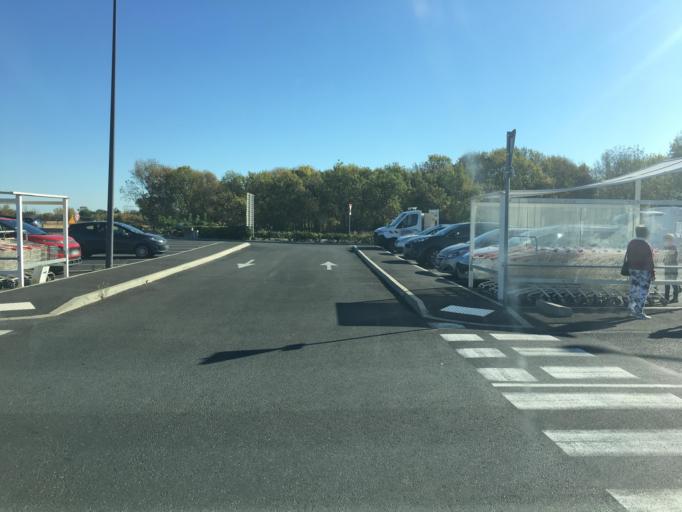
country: FR
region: Languedoc-Roussillon
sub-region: Departement de l'Herault
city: Serignan
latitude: 43.2708
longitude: 3.2831
